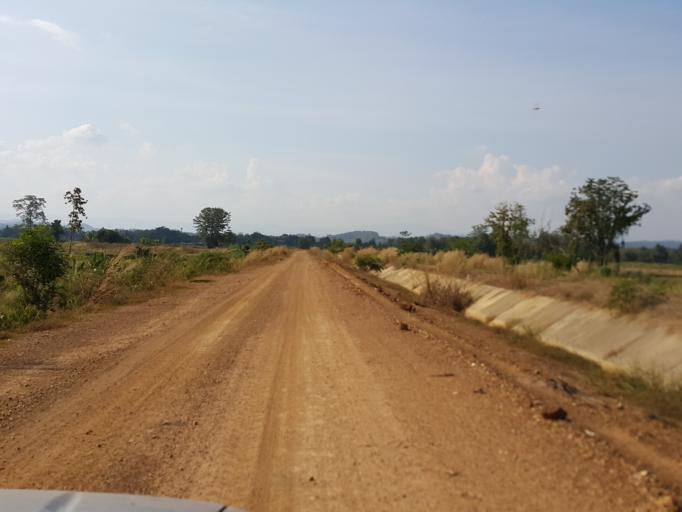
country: TH
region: Sukhothai
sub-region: Amphoe Si Satchanalai
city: Si Satchanalai
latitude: 17.4790
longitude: 99.6567
